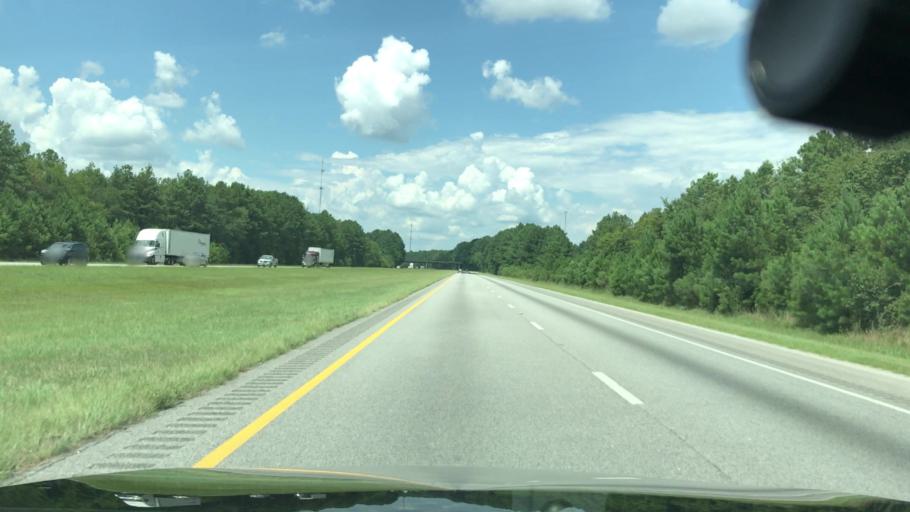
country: US
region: South Carolina
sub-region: Chester County
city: Great Falls
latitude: 34.5305
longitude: -80.9997
